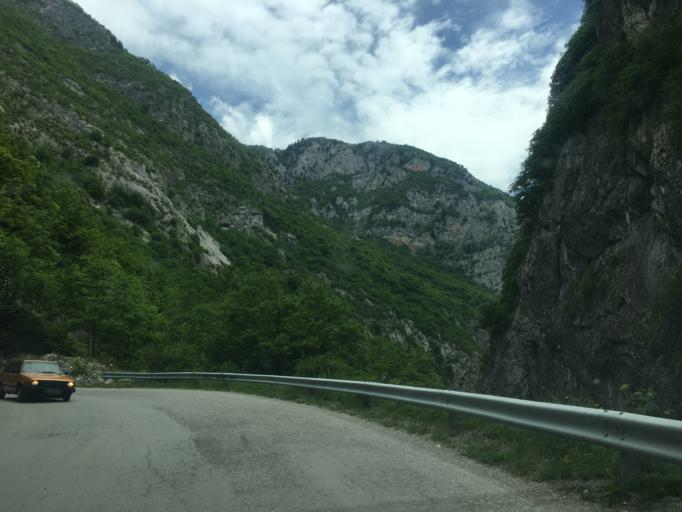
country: XK
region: Pec
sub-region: Komuna e Pejes
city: Peje
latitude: 42.6641
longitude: 20.2222
